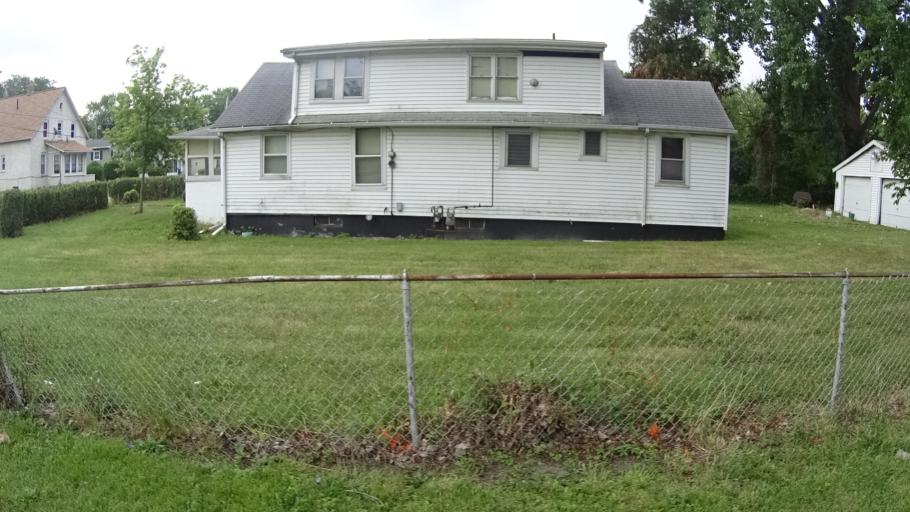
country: US
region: Ohio
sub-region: Erie County
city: Sandusky
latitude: 41.4393
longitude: -82.7238
